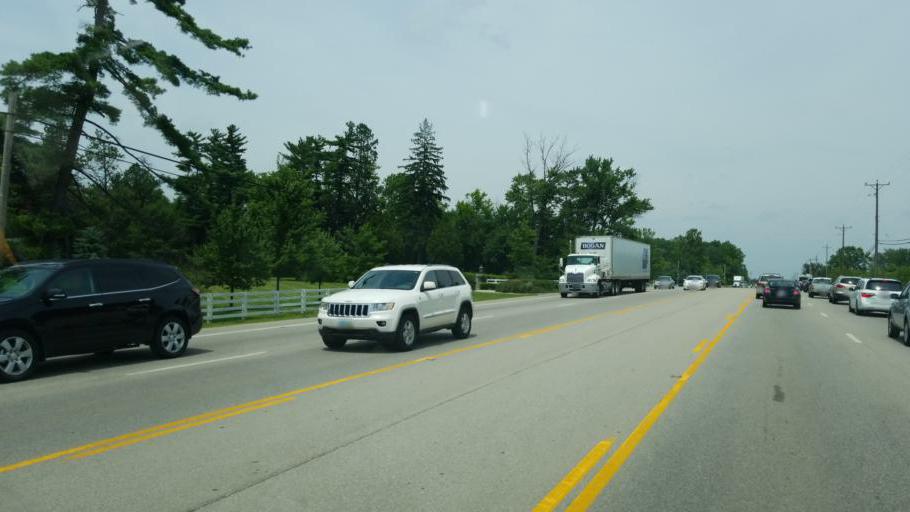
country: US
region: Ohio
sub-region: Franklin County
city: Worthington
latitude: 40.1459
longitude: -83.0177
